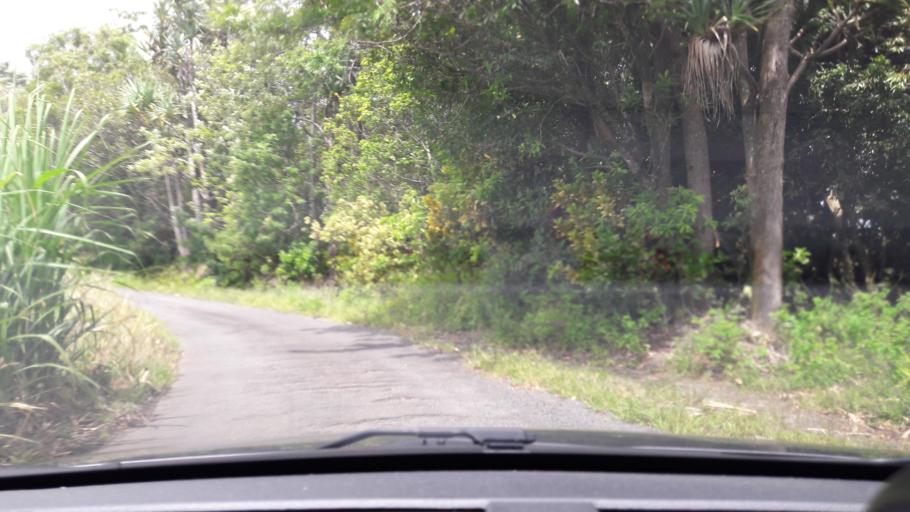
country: RE
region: Reunion
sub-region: Reunion
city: Saint-Benoit
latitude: -21.0978
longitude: 55.6979
